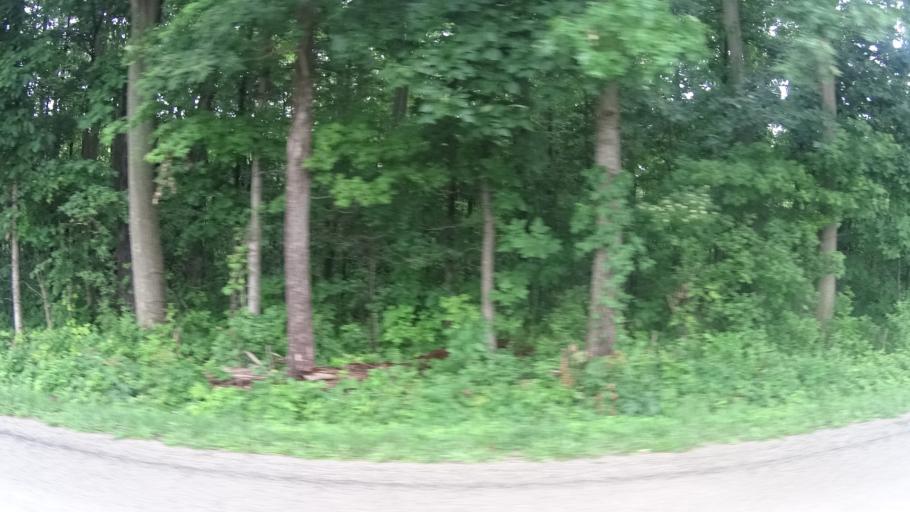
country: US
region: Ohio
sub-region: Erie County
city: Huron
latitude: 41.3531
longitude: -82.5443
